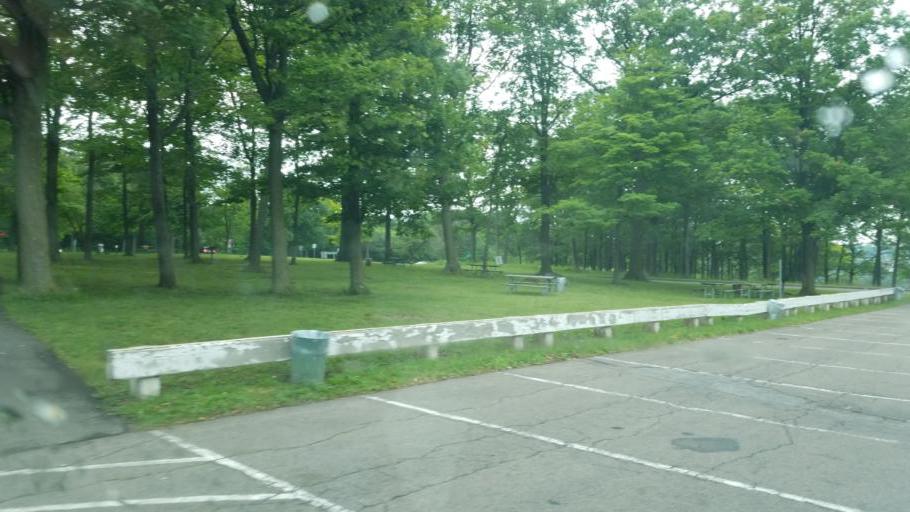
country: CA
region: Ontario
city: Niagara Falls
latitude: 43.1201
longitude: -79.0638
